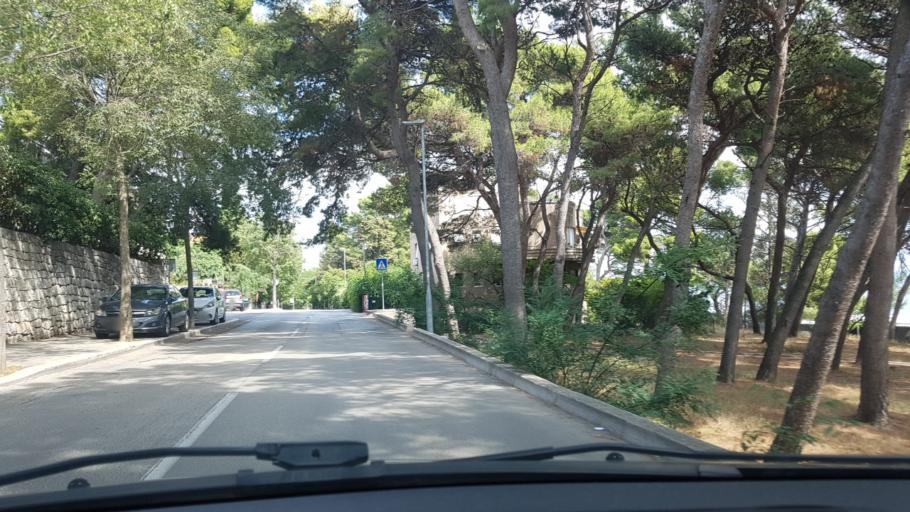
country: HR
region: Splitsko-Dalmatinska
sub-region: Grad Split
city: Split
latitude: 43.5014
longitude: 16.4517
